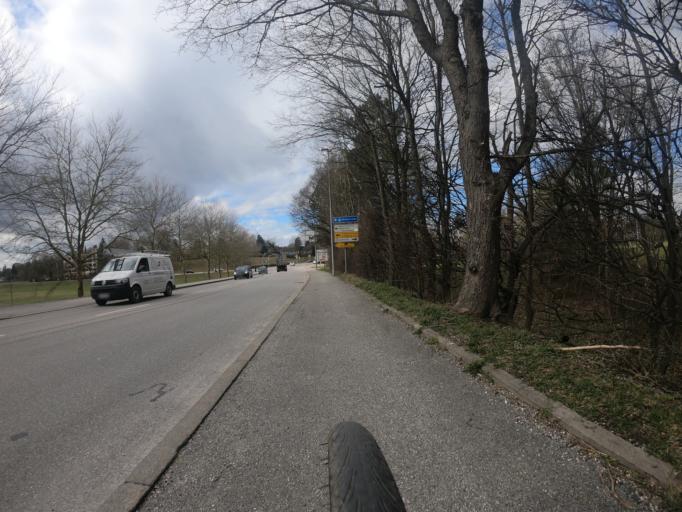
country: DE
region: Bavaria
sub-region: Upper Bavaria
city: Fuerstenfeldbruck
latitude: 48.1713
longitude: 11.2411
